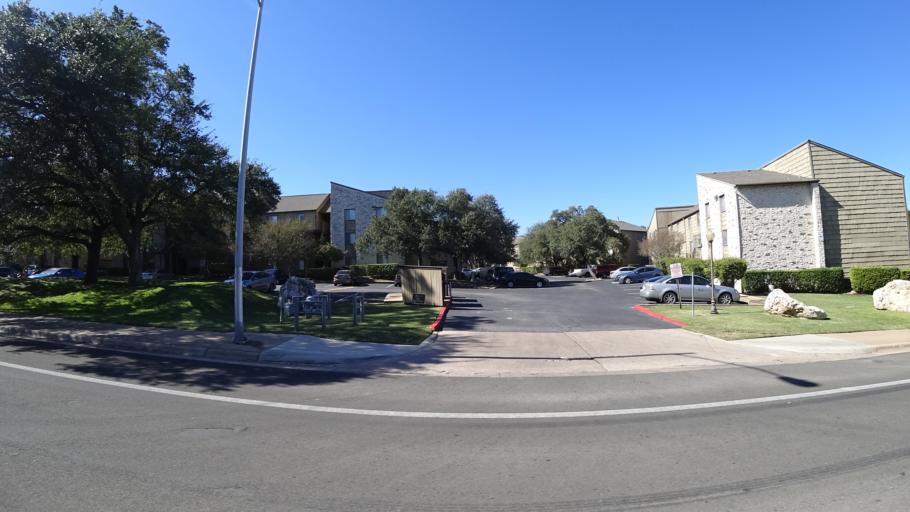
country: US
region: Texas
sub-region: Travis County
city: West Lake Hills
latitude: 30.3593
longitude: -97.7505
